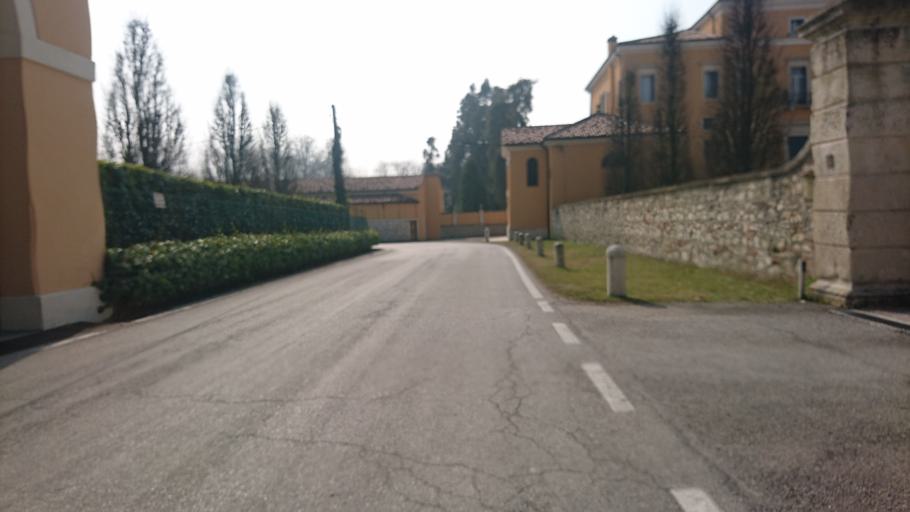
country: IT
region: Veneto
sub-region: Provincia di Vicenza
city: Montegalda
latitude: 45.4502
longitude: 11.6673
